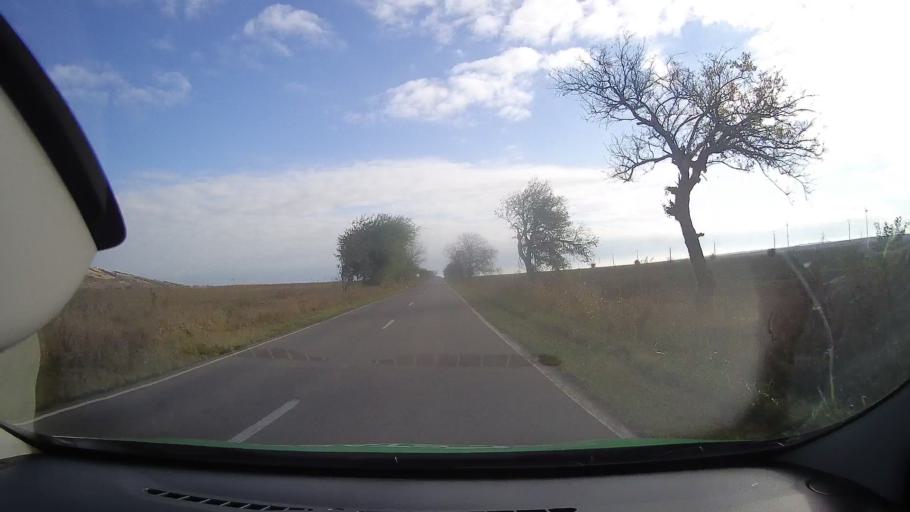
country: RO
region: Tulcea
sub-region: Comuna Mahmudia
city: Mahmudia
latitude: 45.0777
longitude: 29.0573
